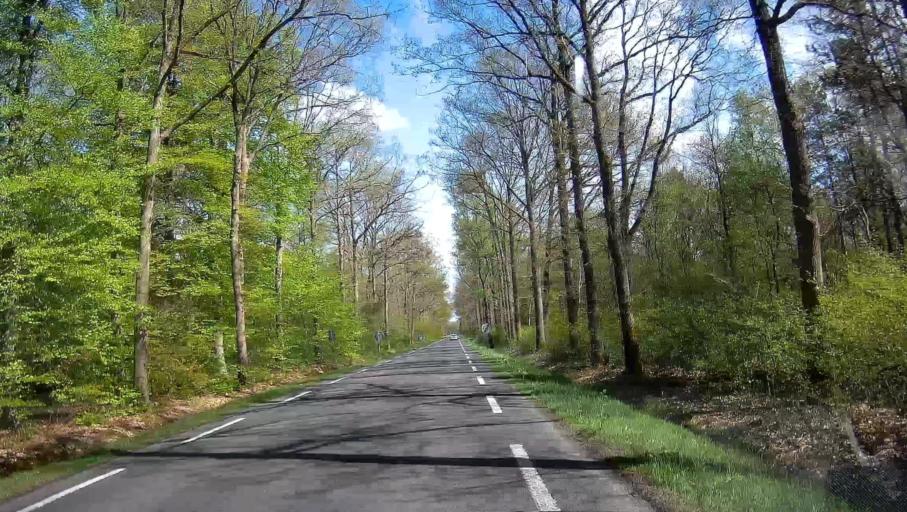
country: NL
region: Drenthe
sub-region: Gemeente Borger-Odoorn
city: Borger
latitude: 52.9447
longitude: 6.7157
